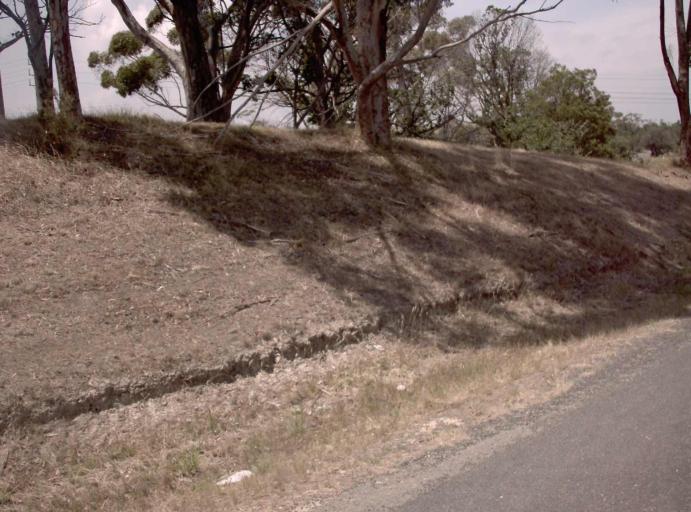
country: AU
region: Victoria
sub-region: Latrobe
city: Traralgon
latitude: -38.2196
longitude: 146.5466
